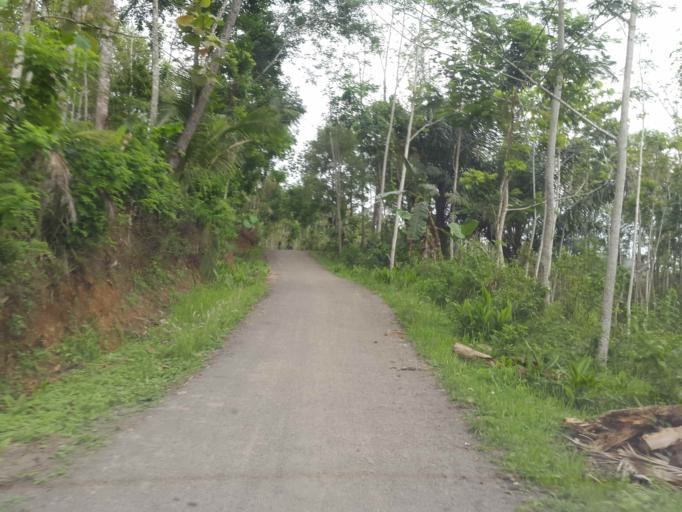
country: ID
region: Central Java
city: Bantarmangu
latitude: -7.3483
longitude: 108.9306
